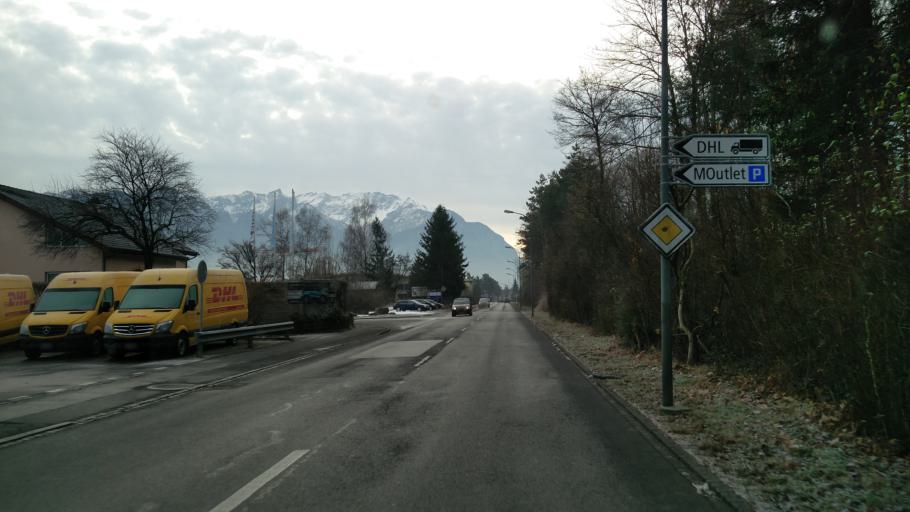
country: CH
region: Saint Gallen
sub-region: Wahlkreis Werdenberg
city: Buchs
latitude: 47.1627
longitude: 9.4783
